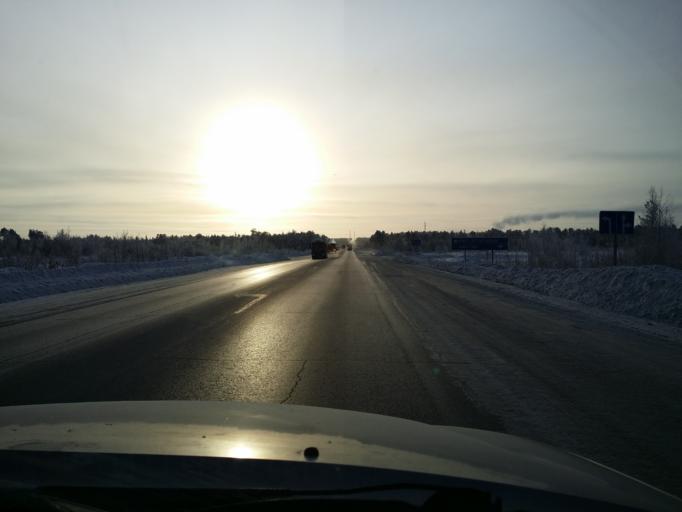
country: RU
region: Khanty-Mansiyskiy Avtonomnyy Okrug
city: Surgut
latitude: 61.4091
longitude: 73.6993
